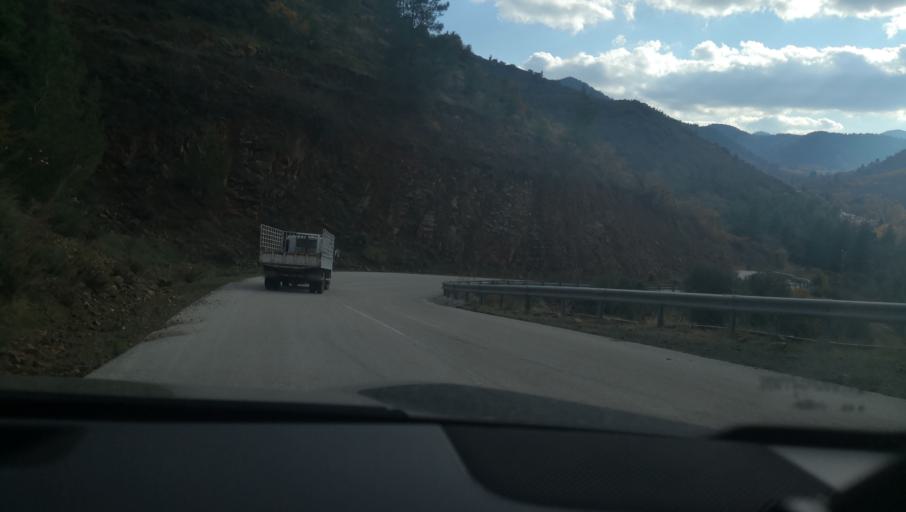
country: CY
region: Lefkosia
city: Lefka
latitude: 35.0478
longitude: 32.7378
